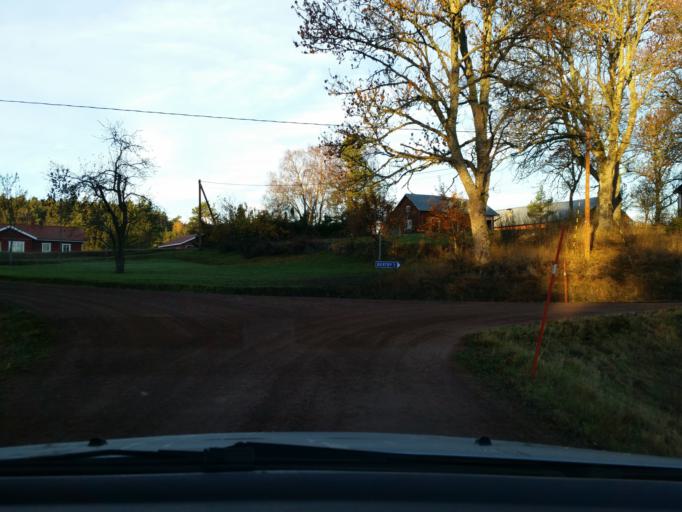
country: AX
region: Alands landsbygd
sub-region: Sund
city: Sund
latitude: 60.2591
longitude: 20.1275
